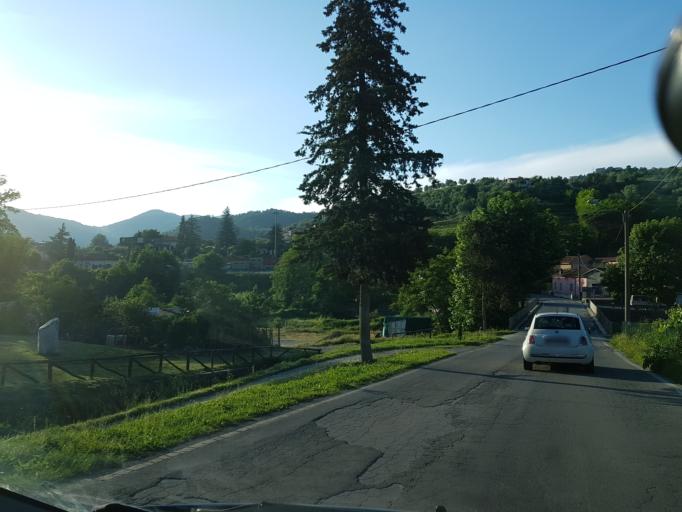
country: IT
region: Tuscany
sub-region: Provincia di Massa-Carrara
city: Casola in Lunigiana
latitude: 44.1928
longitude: 10.1963
